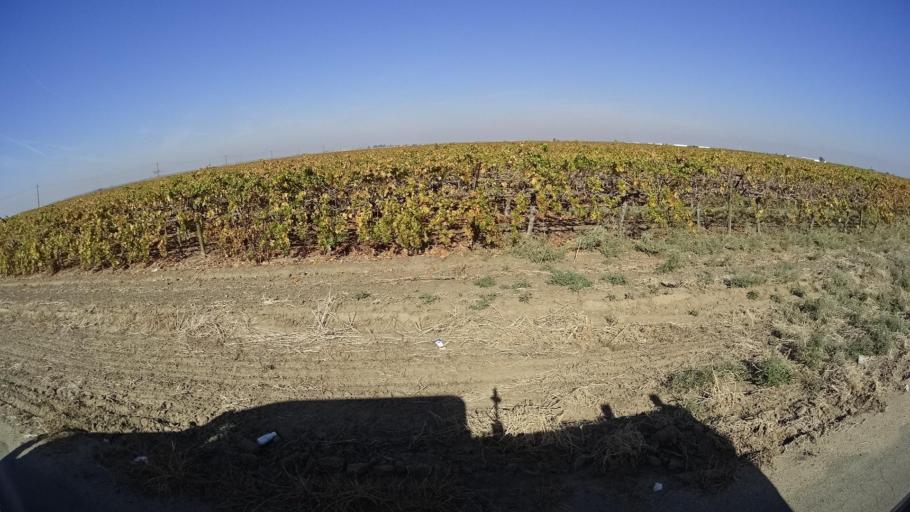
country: US
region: California
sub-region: Kern County
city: McFarland
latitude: 35.7035
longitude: -119.1675
